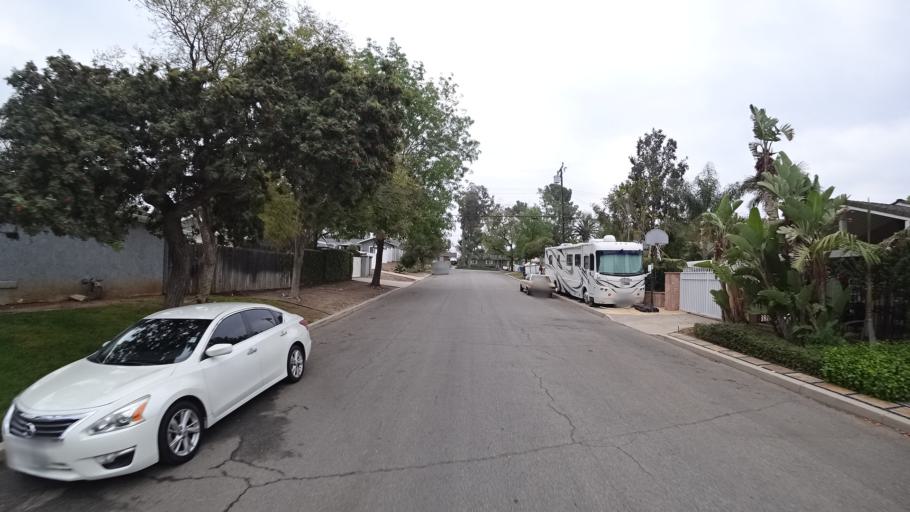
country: US
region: California
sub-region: Ventura County
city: Thousand Oaks
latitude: 34.2070
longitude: -118.8538
